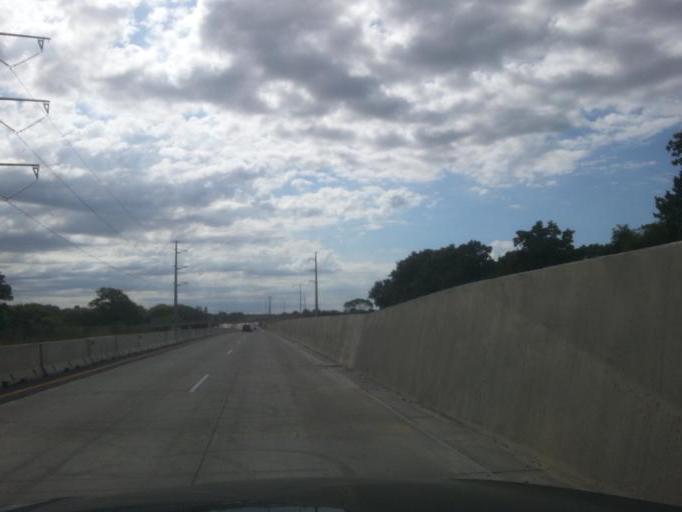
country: US
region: Wisconsin
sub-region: Dane County
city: Shorewood Hills
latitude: 43.0413
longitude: -89.4625
